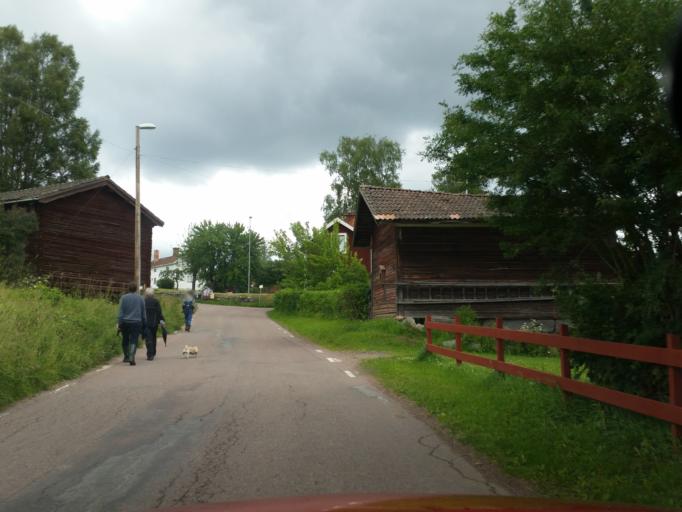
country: SE
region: Dalarna
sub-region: Leksand Municipality
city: Smedby
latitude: 60.7029
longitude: 15.1356
